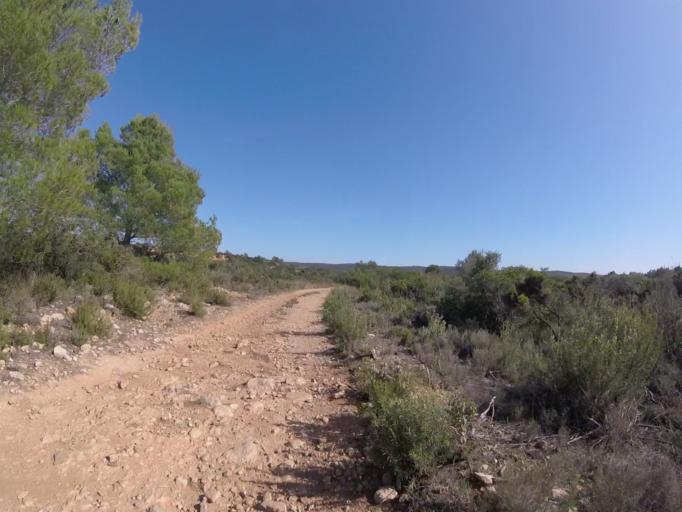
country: ES
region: Valencia
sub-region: Provincia de Castello
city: Cuevas de Vinroma
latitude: 40.2816
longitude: 0.0827
